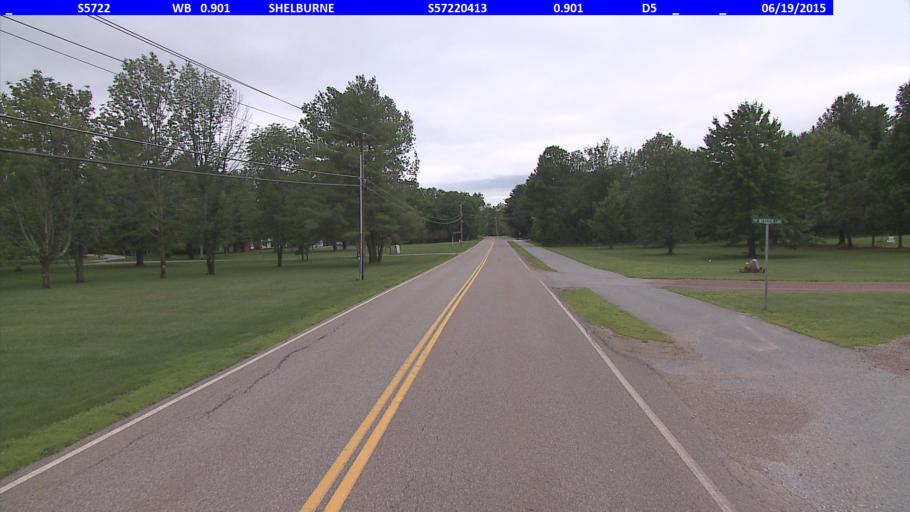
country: US
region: Vermont
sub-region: Chittenden County
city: South Burlington
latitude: 44.3898
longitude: -73.2072
